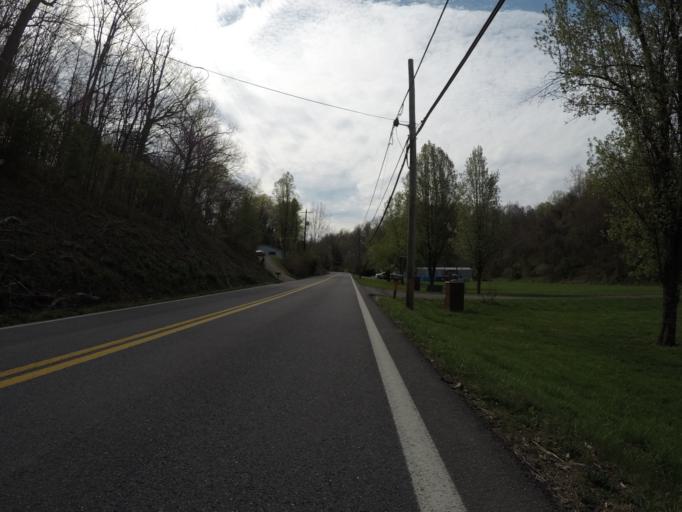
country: US
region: West Virginia
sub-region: Cabell County
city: Pea Ridge
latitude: 38.3794
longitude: -82.3743
